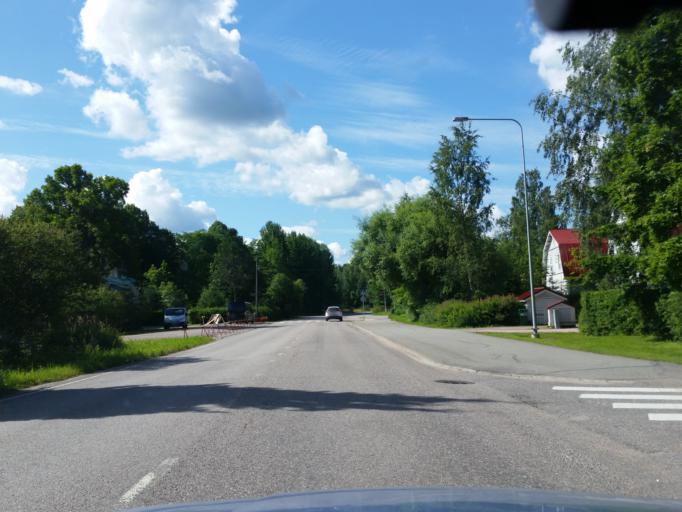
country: FI
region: Uusimaa
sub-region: Helsinki
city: Vihti
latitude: 60.3303
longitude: 24.3171
